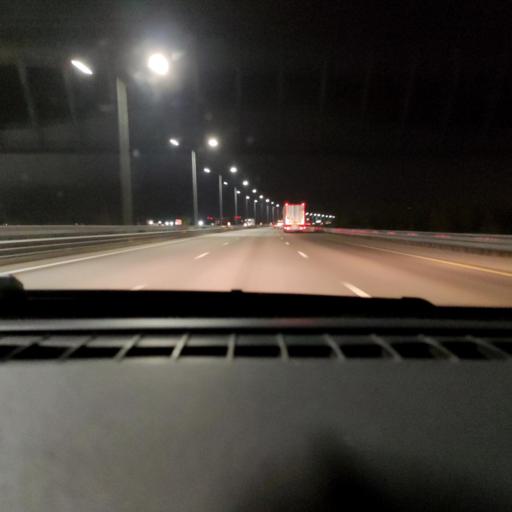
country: RU
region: Voronezj
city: Somovo
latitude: 51.7627
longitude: 39.3064
